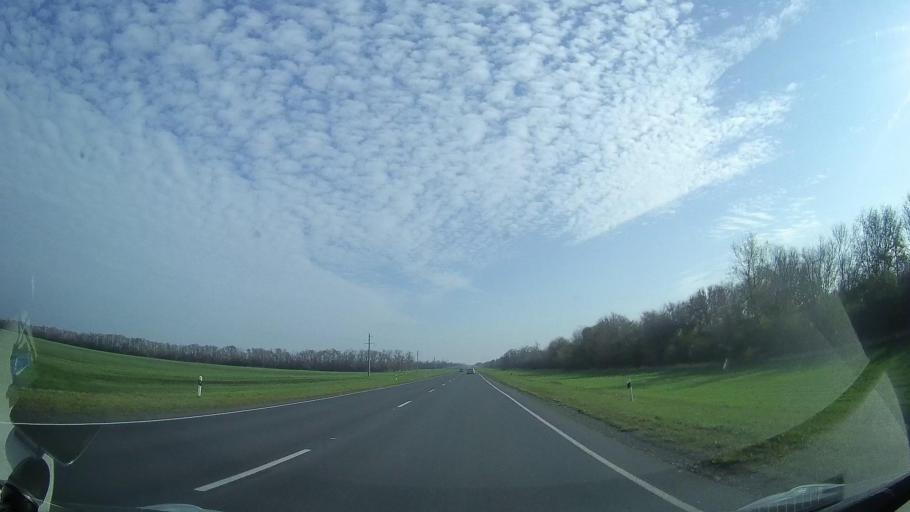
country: RU
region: Rostov
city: Gigant
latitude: 46.5280
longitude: 41.2046
